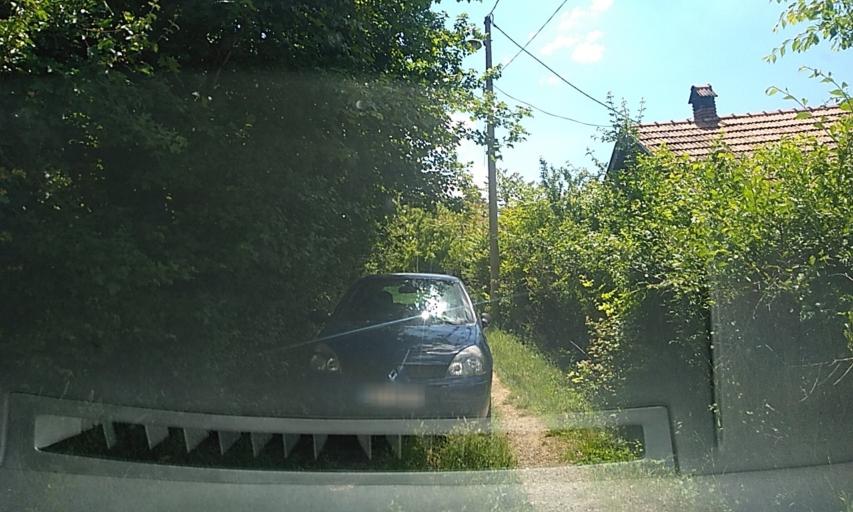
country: RS
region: Central Serbia
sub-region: Nisavski Okrug
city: Niska Banja
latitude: 43.3690
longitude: 21.9962
